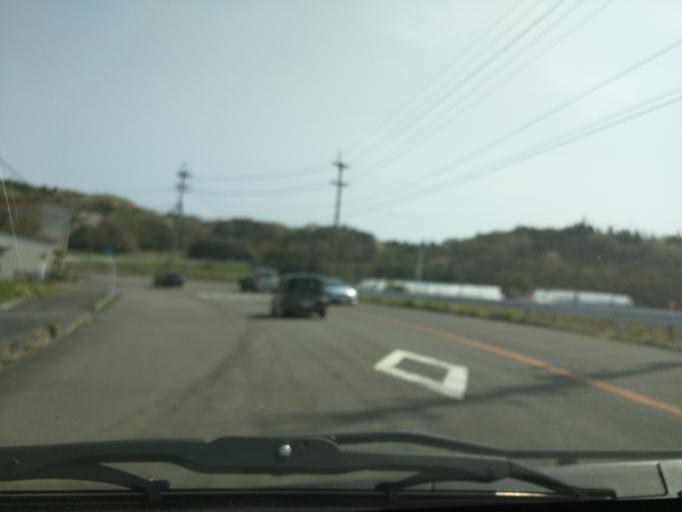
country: JP
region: Fukushima
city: Nihommatsu
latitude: 37.5983
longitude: 140.3823
